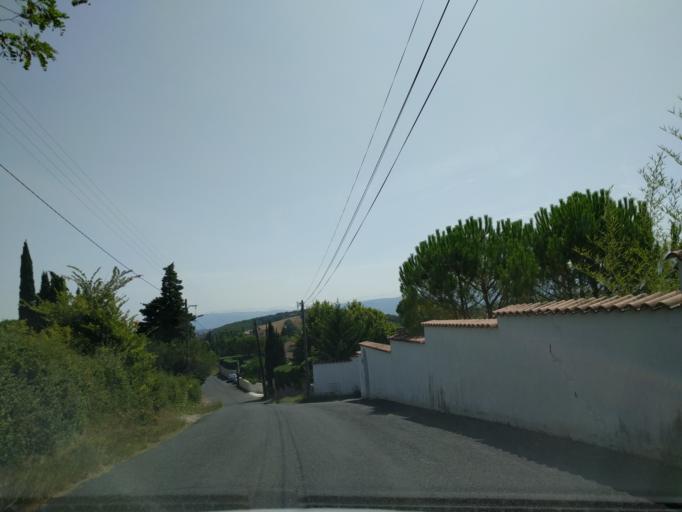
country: FR
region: Midi-Pyrenees
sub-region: Departement du Tarn
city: Castres
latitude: 43.5941
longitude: 2.2586
